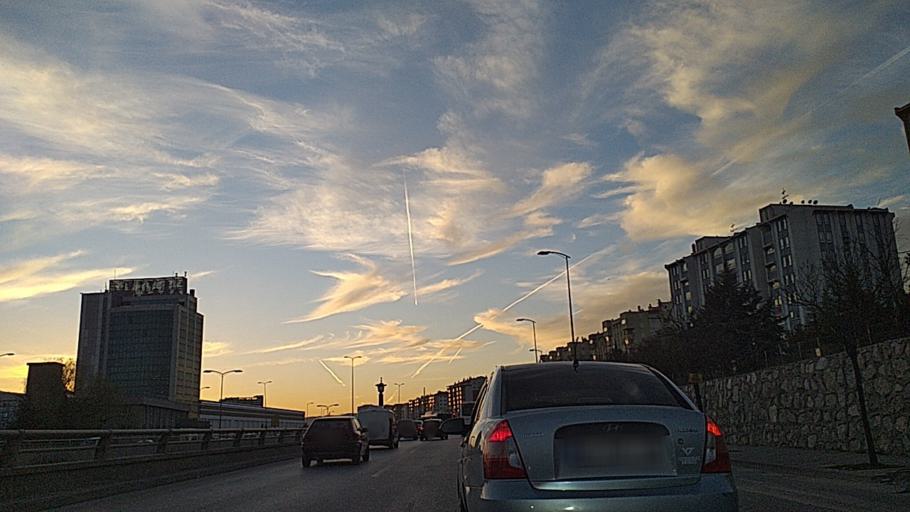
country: TR
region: Ankara
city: Etimesgut
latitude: 39.9677
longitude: 32.6273
